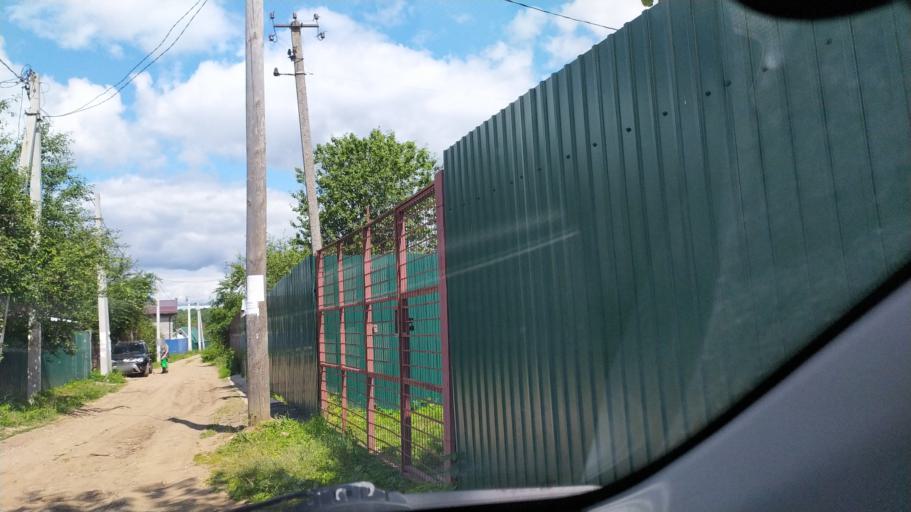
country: RU
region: Chuvashia
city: Novyye Lapsary
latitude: 56.1145
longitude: 47.1749
